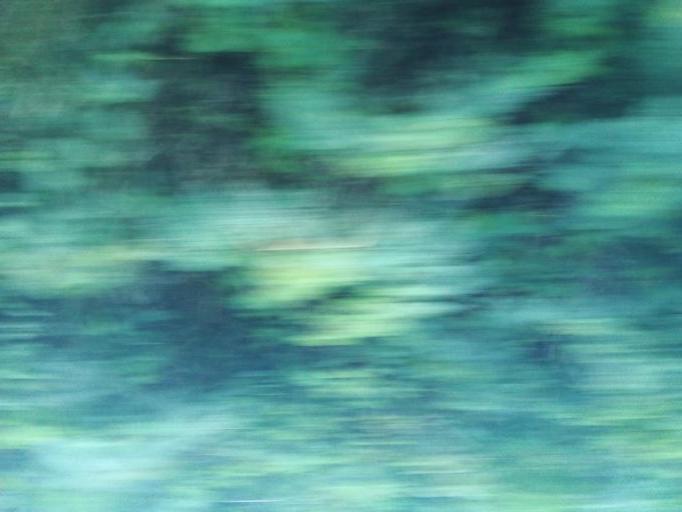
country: BR
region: Minas Gerais
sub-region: Joao Monlevade
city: Joao Monlevade
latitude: -19.8252
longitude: -43.1039
